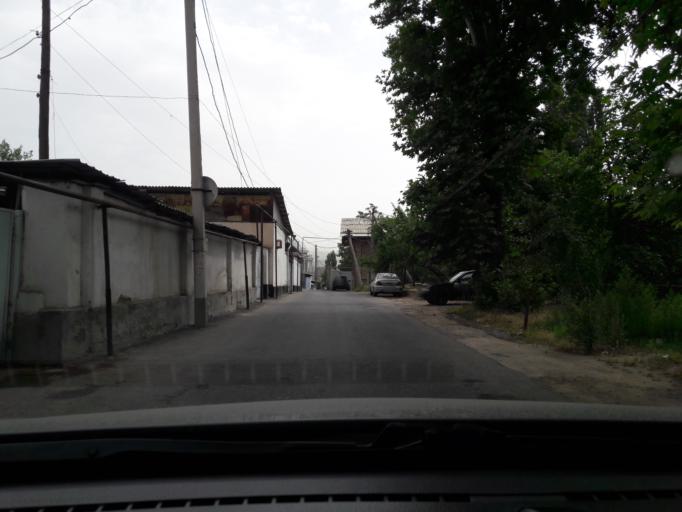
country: TJ
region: Dushanbe
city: Dushanbe
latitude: 38.5789
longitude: 68.7629
